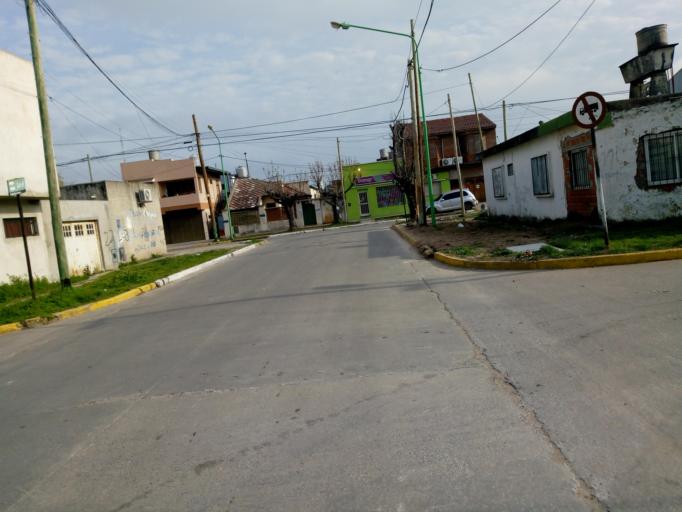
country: AR
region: Buenos Aires
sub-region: Partido de La Plata
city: La Plata
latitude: -34.8965
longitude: -57.9373
